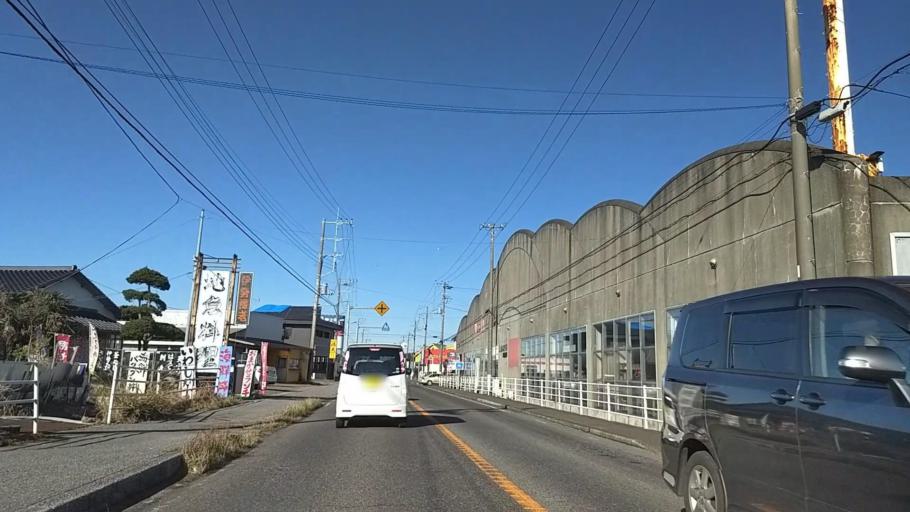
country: JP
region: Chiba
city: Ohara
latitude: 35.2795
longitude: 140.3935
